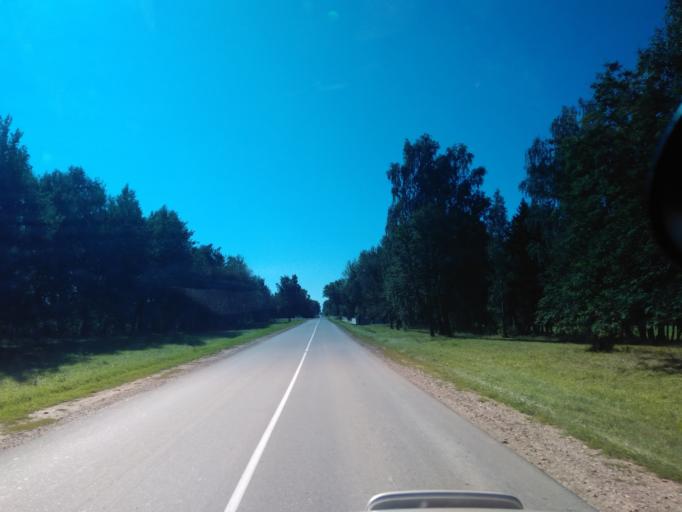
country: BY
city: Fanipol
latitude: 53.7130
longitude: 27.3450
